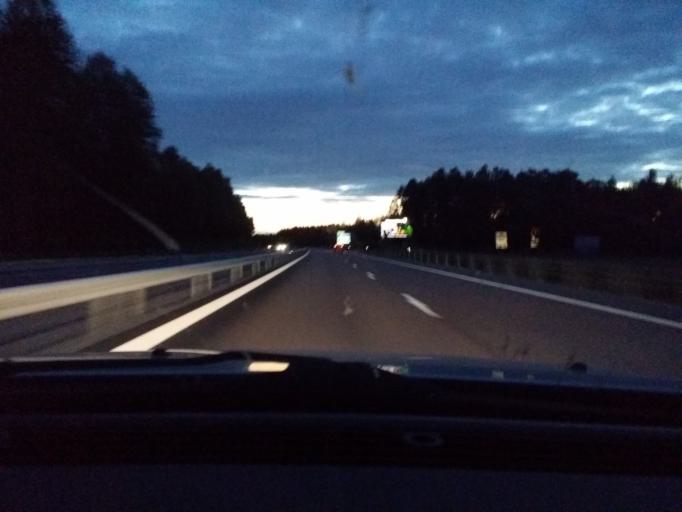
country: SE
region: Vaestmanland
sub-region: Vasteras
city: Tillberga
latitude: 59.6241
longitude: 16.6838
